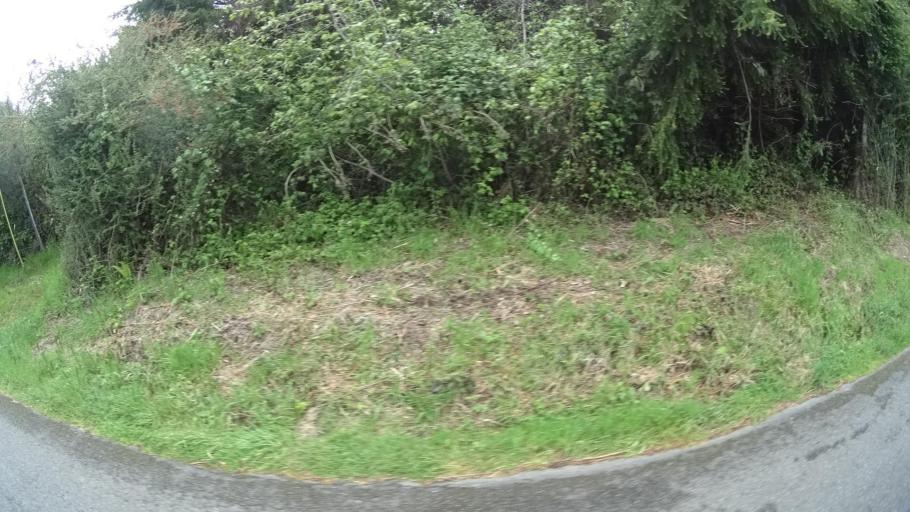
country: US
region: California
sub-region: Humboldt County
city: Bayside
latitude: 40.8419
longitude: -124.0247
